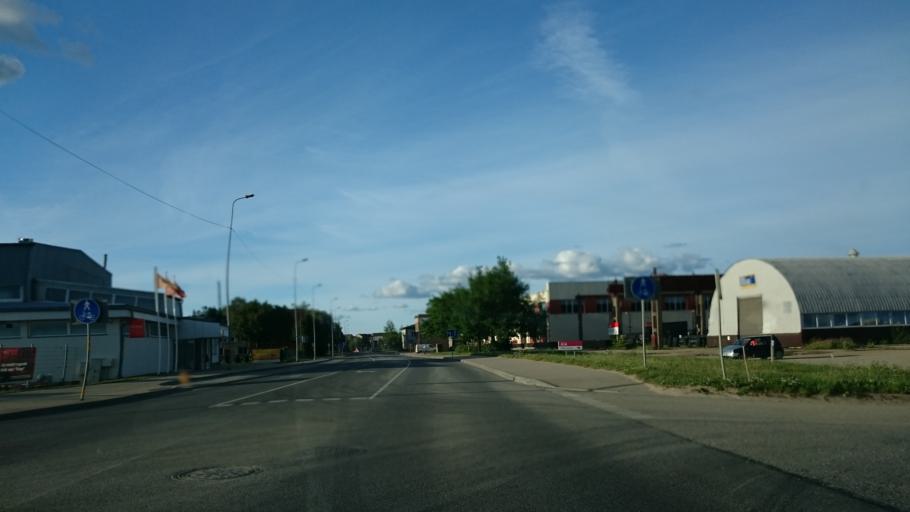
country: LV
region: Saldus Rajons
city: Saldus
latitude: 56.6584
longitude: 22.4742
